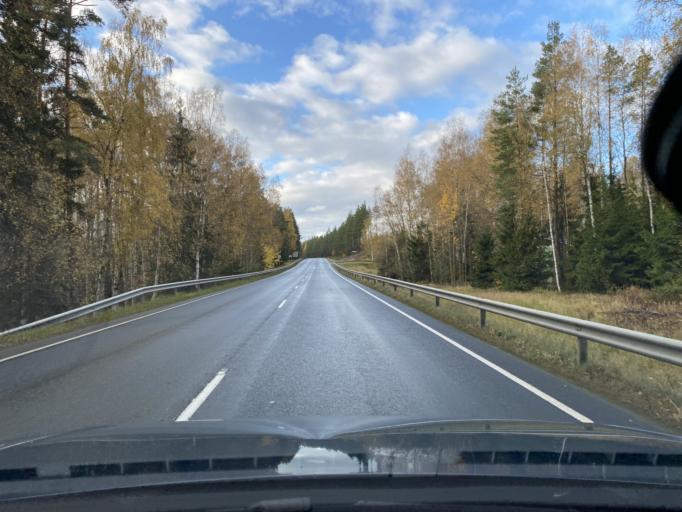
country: FI
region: Haeme
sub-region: Forssa
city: Humppila
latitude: 60.9705
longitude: 23.2759
